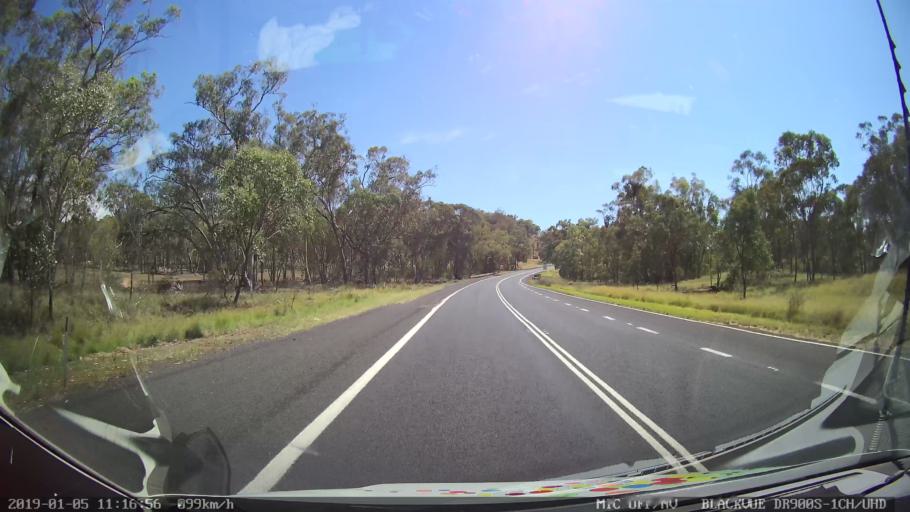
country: AU
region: New South Wales
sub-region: Warrumbungle Shire
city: Coonabarabran
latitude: -31.3321
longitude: 149.3019
